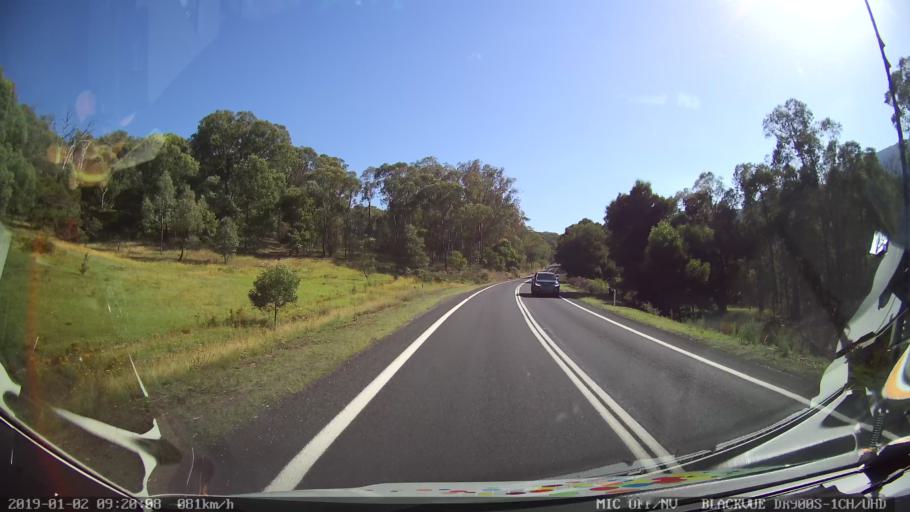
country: AU
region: New South Wales
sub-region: Tumut Shire
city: Tumut
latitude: -35.4149
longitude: 148.2808
